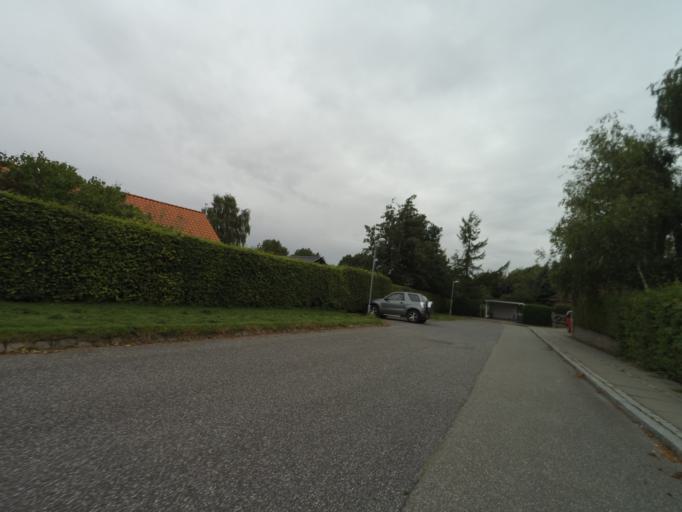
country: DK
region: Central Jutland
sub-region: Arhus Kommune
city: Stavtrup
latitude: 56.1656
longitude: 10.1580
